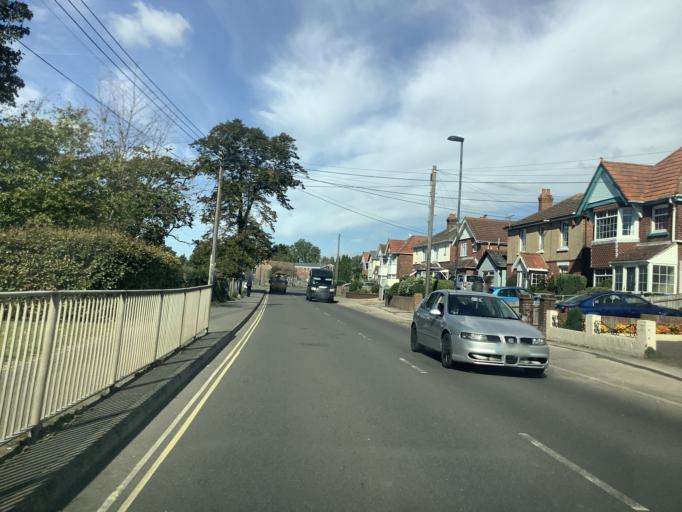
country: GB
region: England
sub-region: Hampshire
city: Marchwood
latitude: 50.9195
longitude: -1.4568
